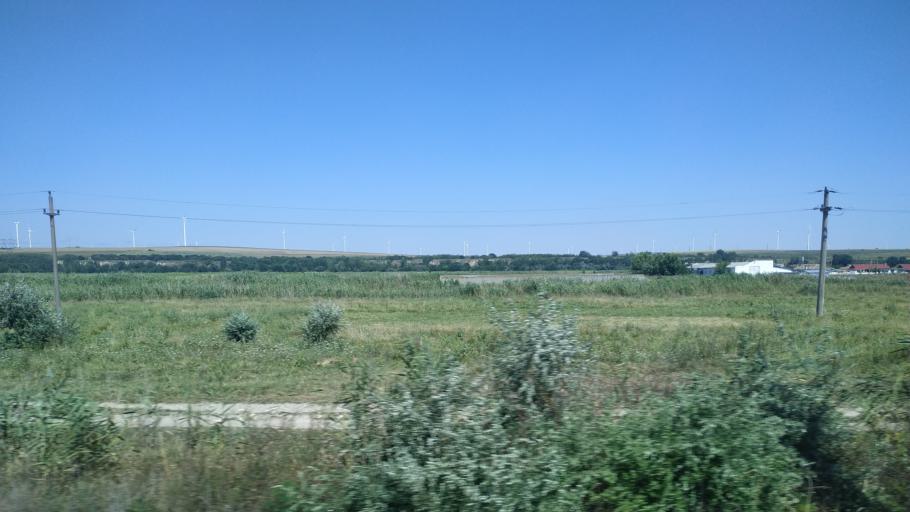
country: RO
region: Constanta
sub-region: Comuna Saligny
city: Faclia
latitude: 44.2679
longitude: 28.1331
